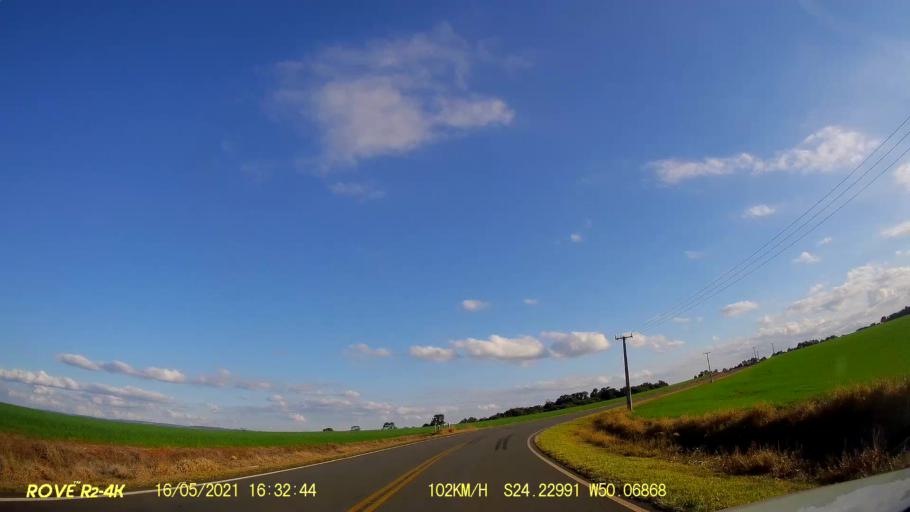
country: BR
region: Parana
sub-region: Pirai Do Sul
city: Pirai do Sul
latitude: -24.2297
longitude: -50.0685
